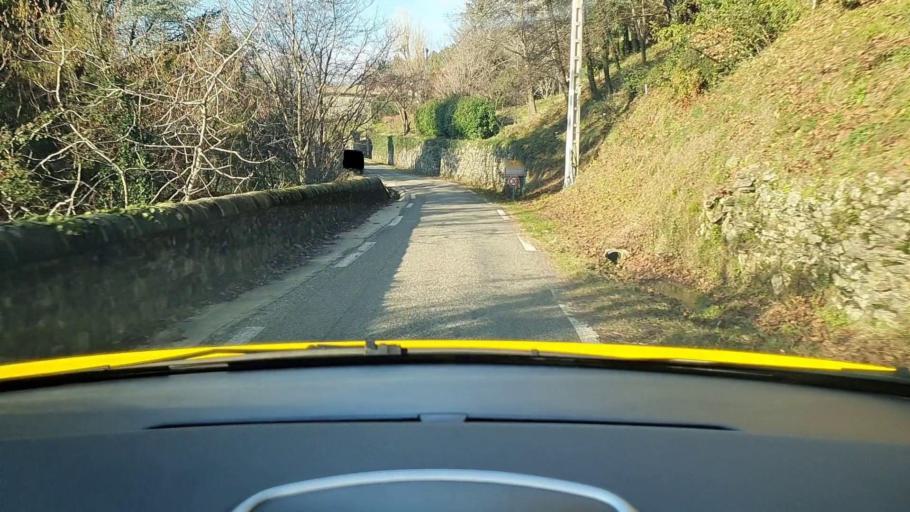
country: FR
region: Languedoc-Roussillon
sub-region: Departement du Gard
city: Branoux-les-Taillades
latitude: 44.3152
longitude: 3.9918
